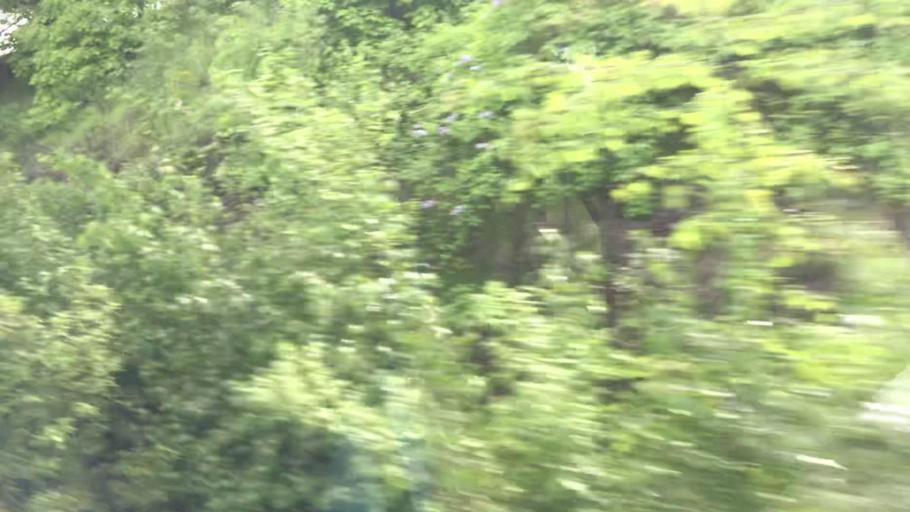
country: PL
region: Lower Silesian Voivodeship
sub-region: Powiat walbrzyski
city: Walbrzych
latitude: 50.7645
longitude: 16.2524
